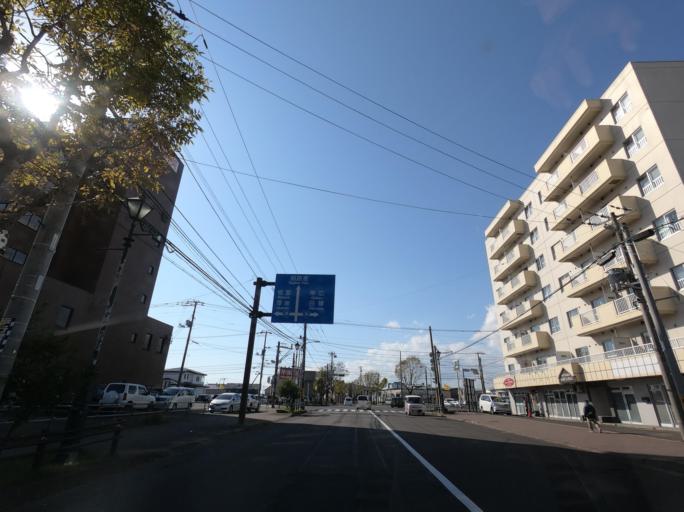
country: JP
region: Hokkaido
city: Kushiro
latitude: 42.9891
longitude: 144.3768
